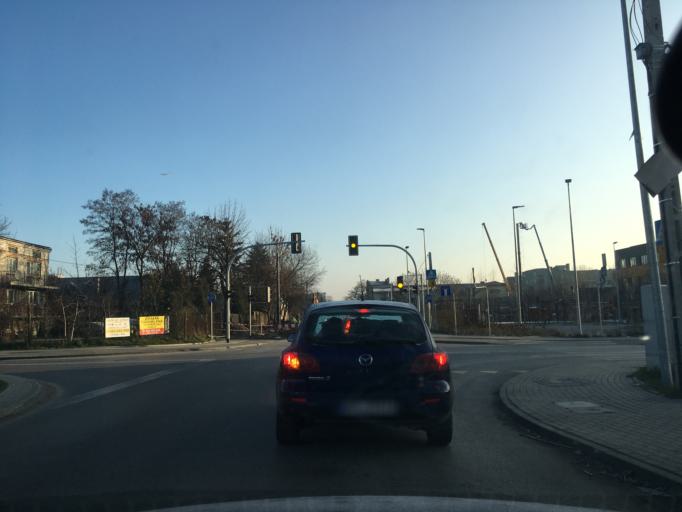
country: PL
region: Masovian Voivodeship
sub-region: Powiat piaseczynski
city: Piaseczno
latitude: 52.0742
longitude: 21.0125
